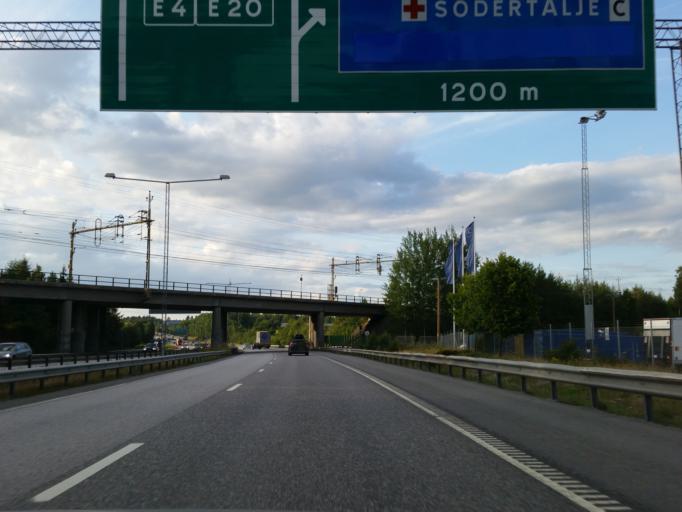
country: SE
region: Stockholm
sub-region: Sodertalje Kommun
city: Pershagen
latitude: 59.1650
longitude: 17.6499
